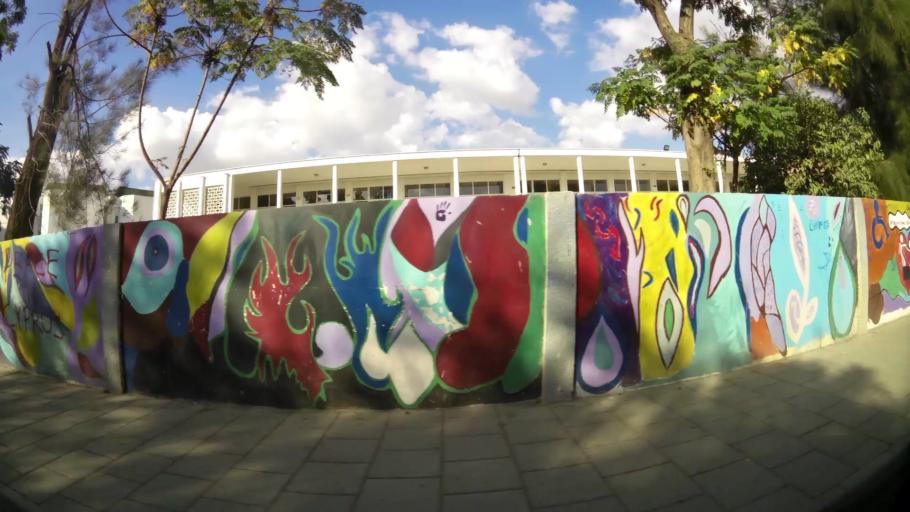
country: CY
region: Lefkosia
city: Nicosia
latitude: 35.1920
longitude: 33.3639
